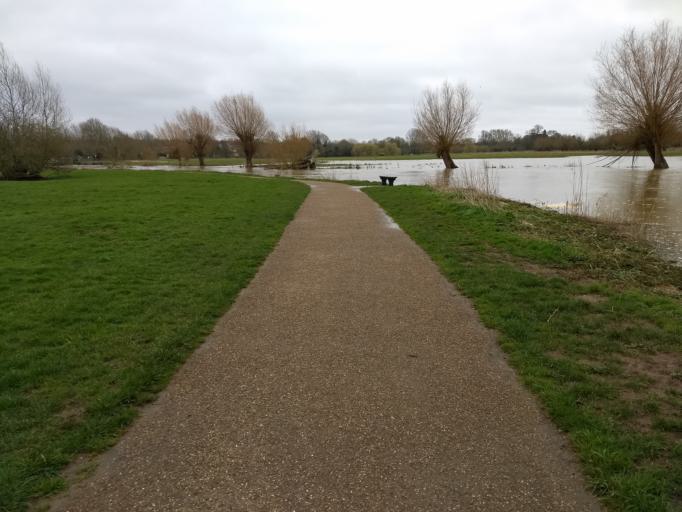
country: GB
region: England
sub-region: Milton Keynes
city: Stony Stratford
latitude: 52.0535
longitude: -0.8583
